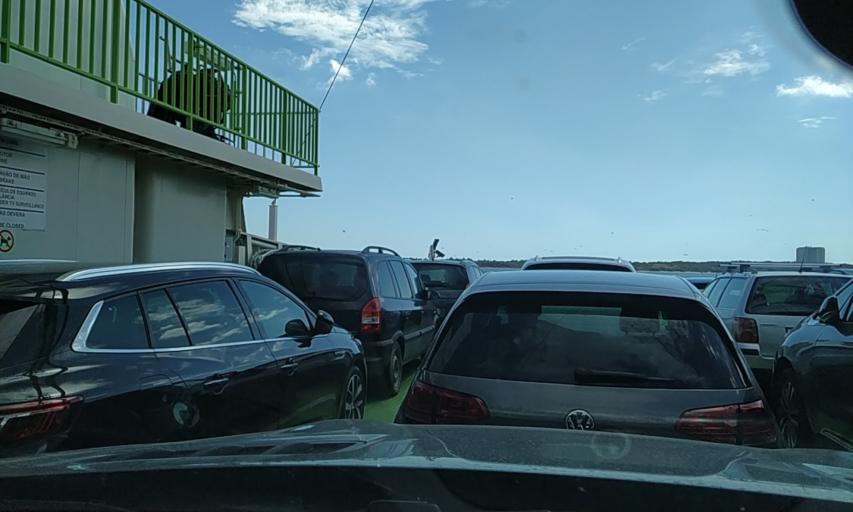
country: PT
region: Setubal
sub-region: Setubal
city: Setubal
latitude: 38.5004
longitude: -8.8873
